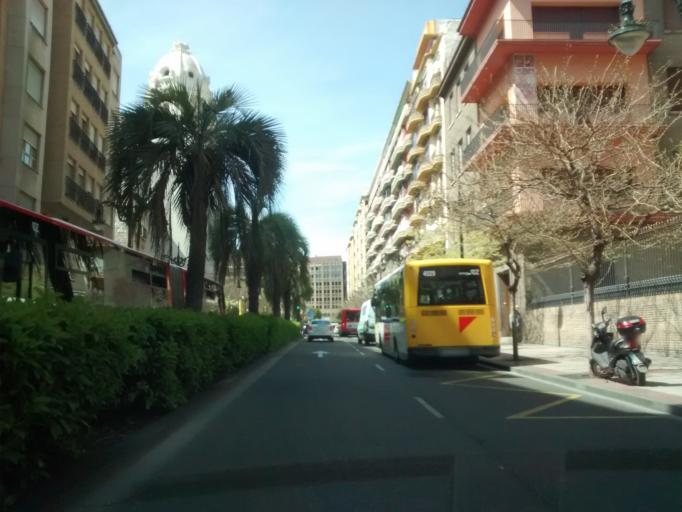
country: ES
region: Aragon
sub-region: Provincia de Zaragoza
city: Almozara
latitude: 41.6558
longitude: -0.8911
